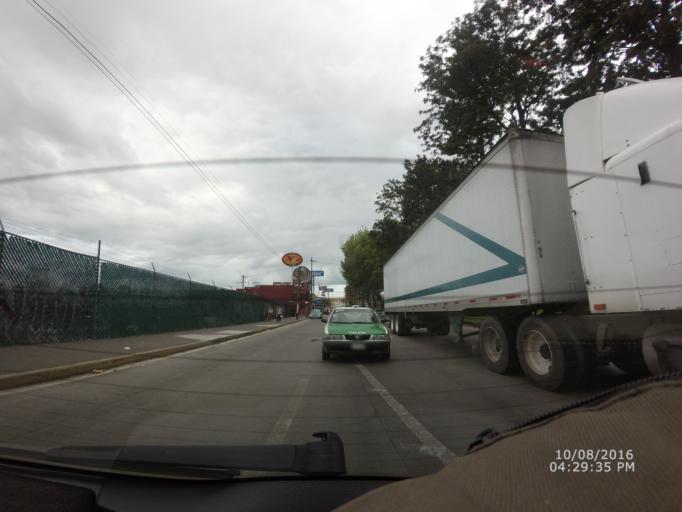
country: MX
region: Veracruz
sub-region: Xalapa
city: Xalapa de Enriquez
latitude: 19.5438
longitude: -96.9092
